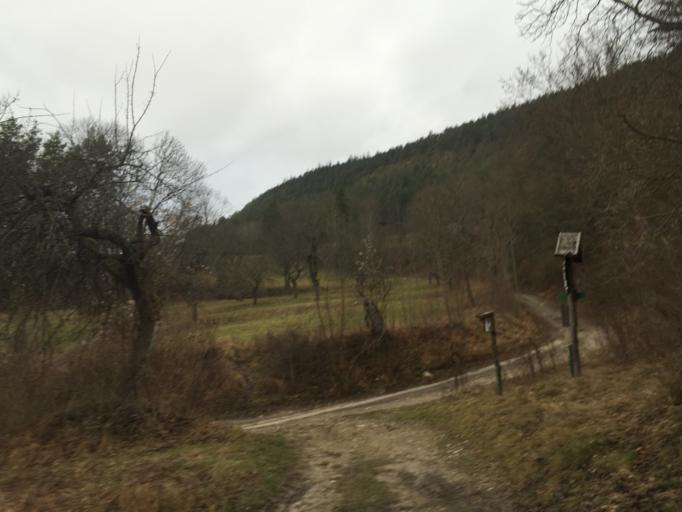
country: DE
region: Thuringia
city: Bad Blankenburg
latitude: 50.7014
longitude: 11.2508
